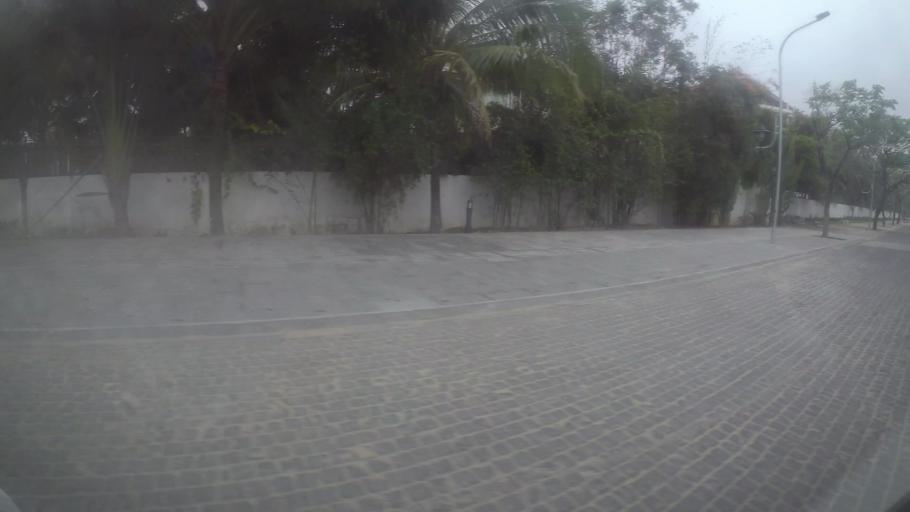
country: VN
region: Da Nang
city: Ngu Hanh Son
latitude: 16.0420
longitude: 108.2512
